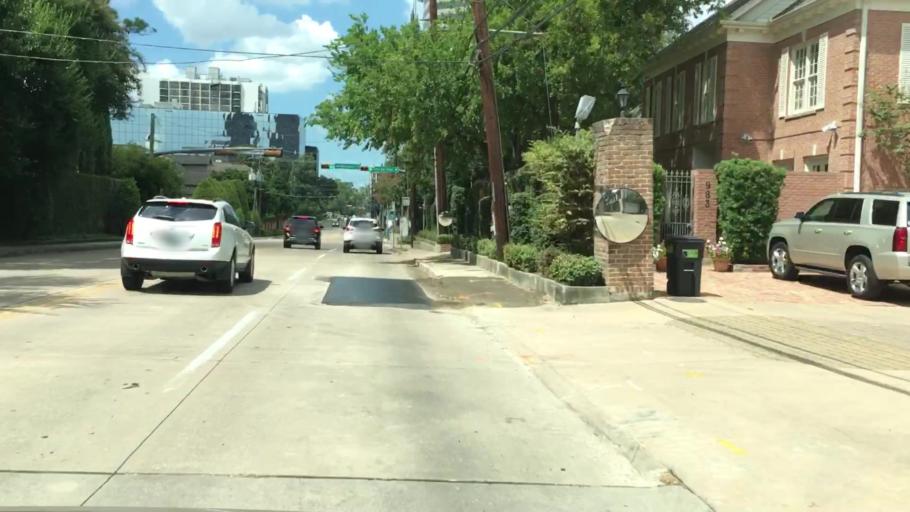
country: US
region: Texas
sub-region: Harris County
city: Hunters Creek Village
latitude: 29.7583
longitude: -95.4632
